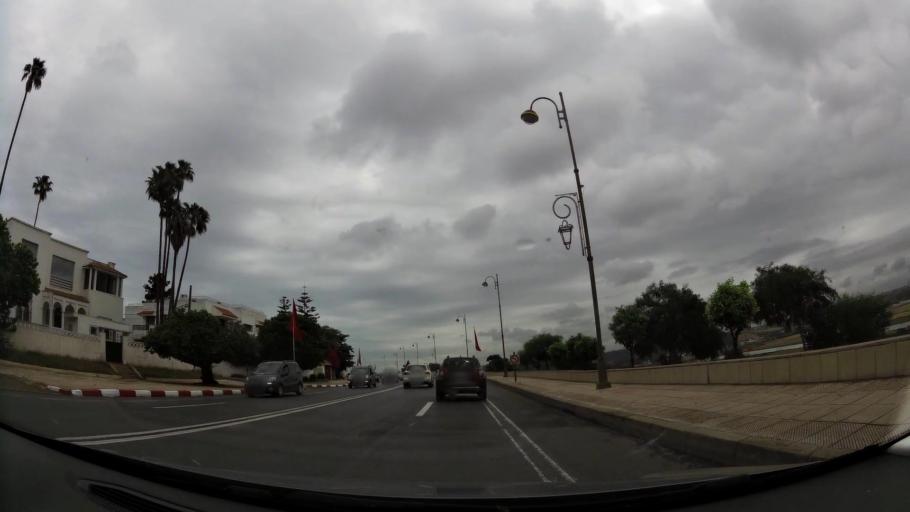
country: MA
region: Rabat-Sale-Zemmour-Zaer
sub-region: Rabat
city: Rabat
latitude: 34.0118
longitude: -6.8208
